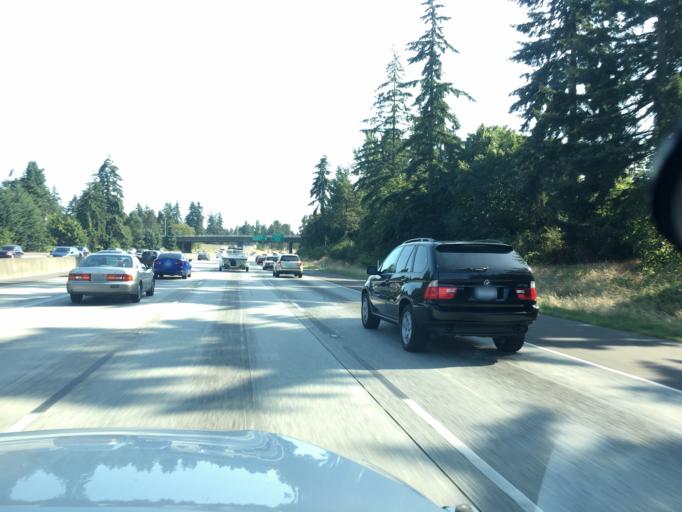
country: US
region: Washington
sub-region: King County
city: Shoreline
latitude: 47.7656
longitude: -122.3232
